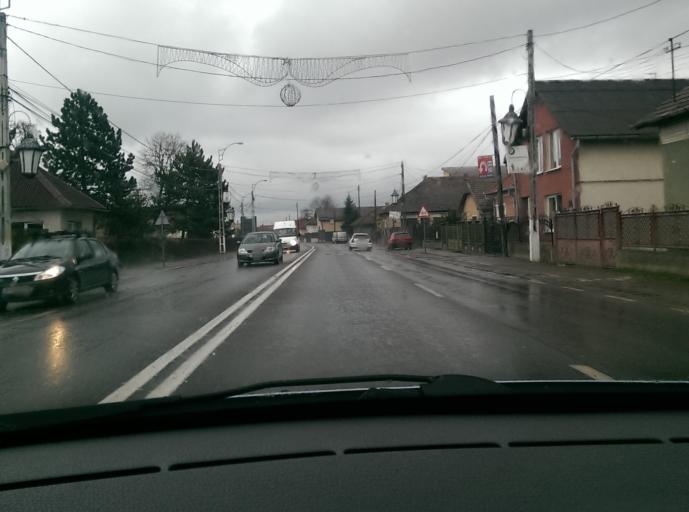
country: RO
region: Cluj
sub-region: Comuna Floresti
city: Floresti
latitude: 46.7444
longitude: 23.4862
